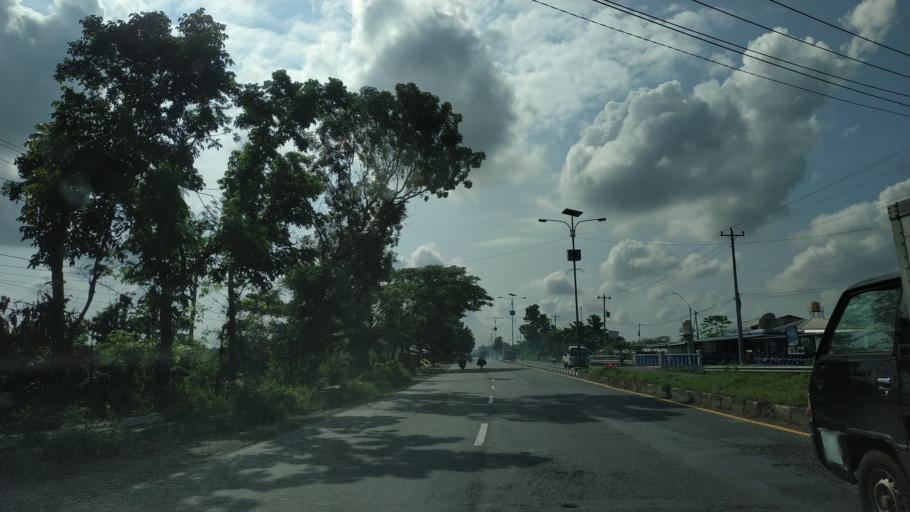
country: ID
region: Central Java
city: Comal
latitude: -6.9004
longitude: 109.5104
